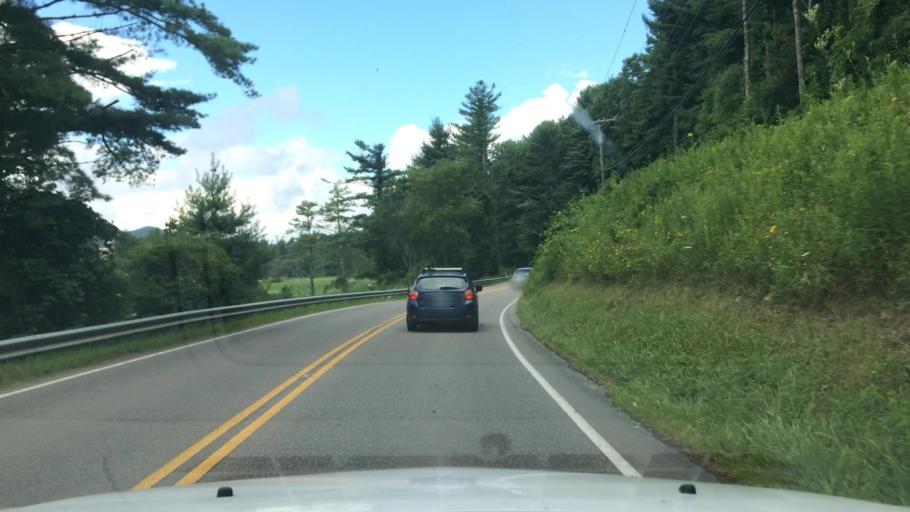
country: US
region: North Carolina
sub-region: Watauga County
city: Boone
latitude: 36.2011
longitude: -81.6431
